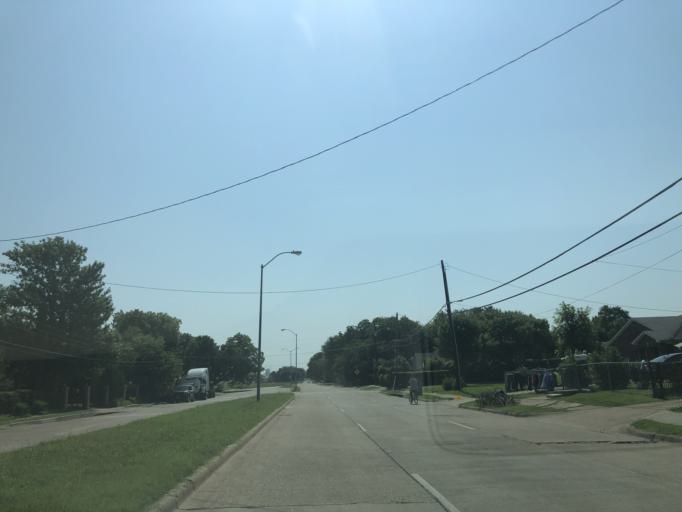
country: US
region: Texas
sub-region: Dallas County
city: Cockrell Hill
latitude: 32.7926
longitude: -96.8694
